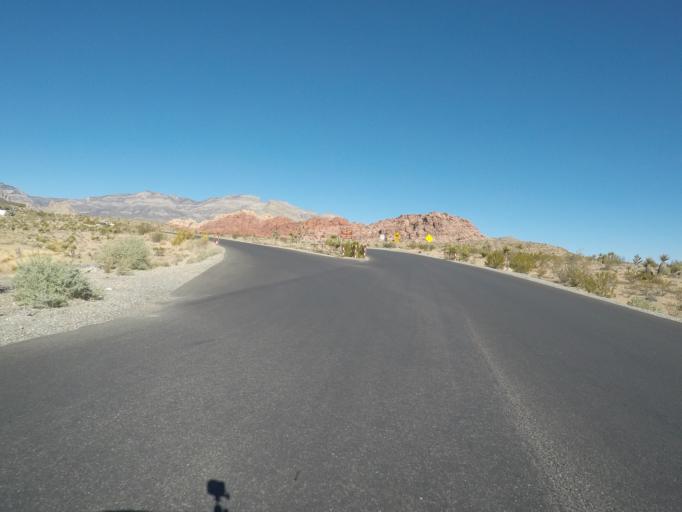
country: US
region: Nevada
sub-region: Clark County
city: Summerlin South
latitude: 36.1341
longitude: -115.4241
